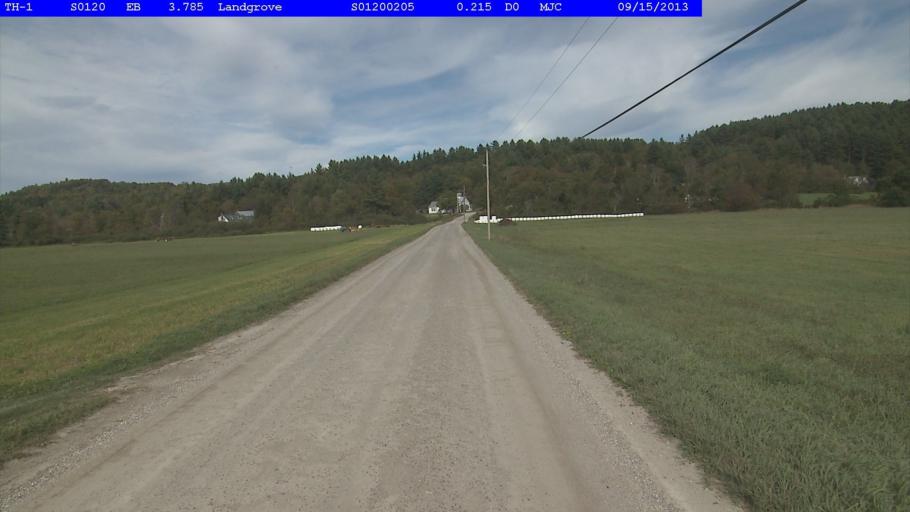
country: US
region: Vermont
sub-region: Bennington County
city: Manchester Center
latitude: 43.2644
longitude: -72.8599
